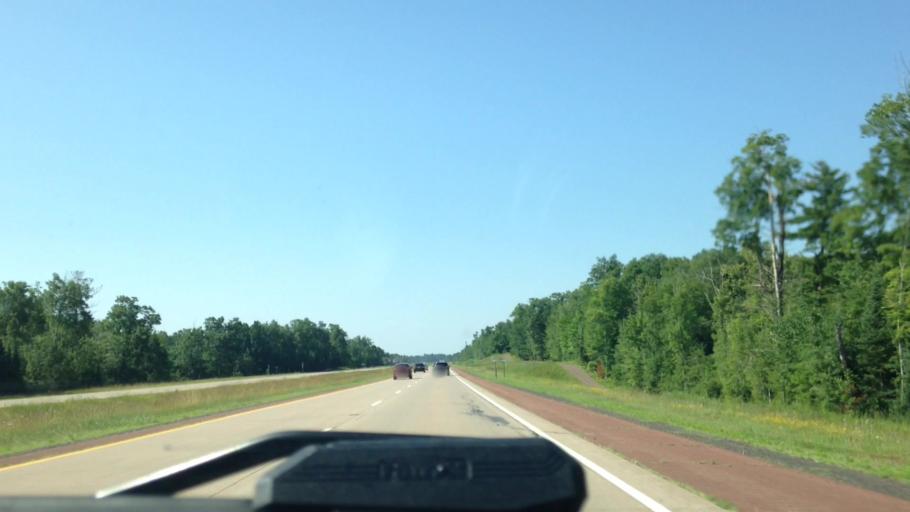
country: US
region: Wisconsin
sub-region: Douglas County
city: Lake Nebagamon
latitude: 46.3769
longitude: -91.8252
